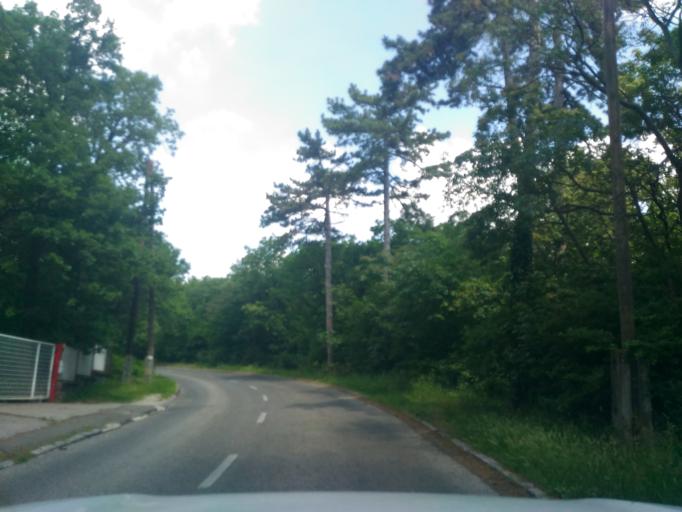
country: HU
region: Baranya
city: Pecs
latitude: 46.0913
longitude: 18.2294
